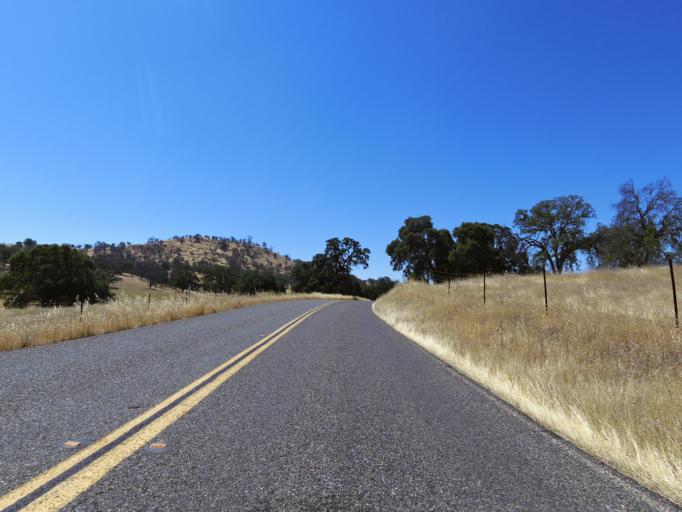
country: US
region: California
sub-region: Mariposa County
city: Mariposa
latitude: 37.4851
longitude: -120.1359
